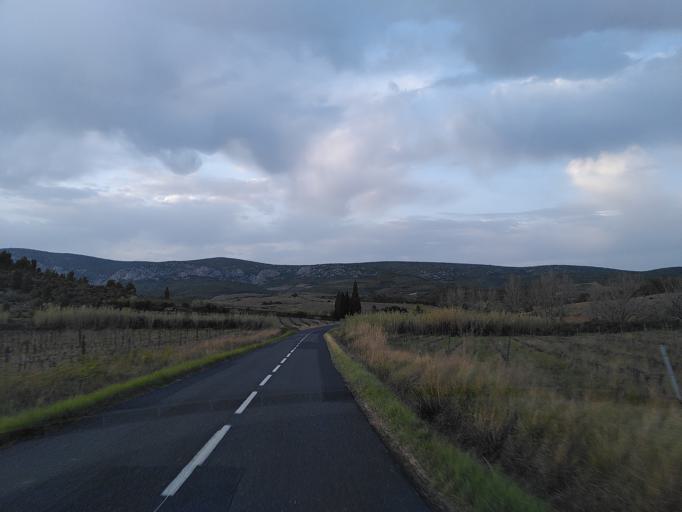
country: FR
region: Languedoc-Roussillon
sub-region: Departement des Pyrenees-Orientales
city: Estagel
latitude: 42.8111
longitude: 2.6990
